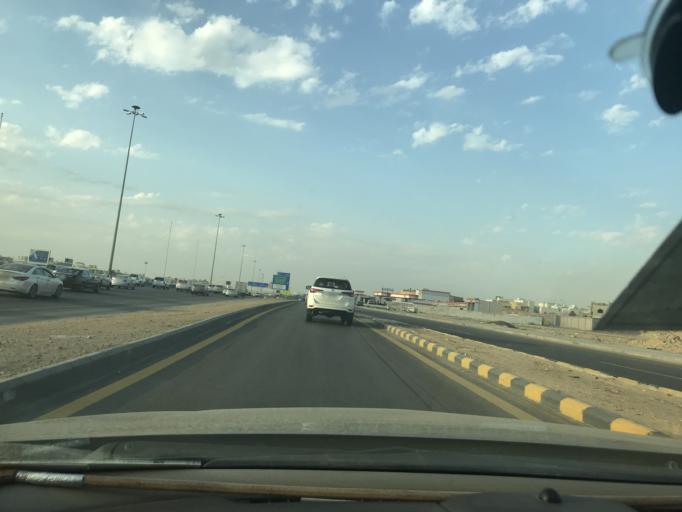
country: SA
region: Ar Riyad
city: Riyadh
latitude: 24.7451
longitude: 46.5857
